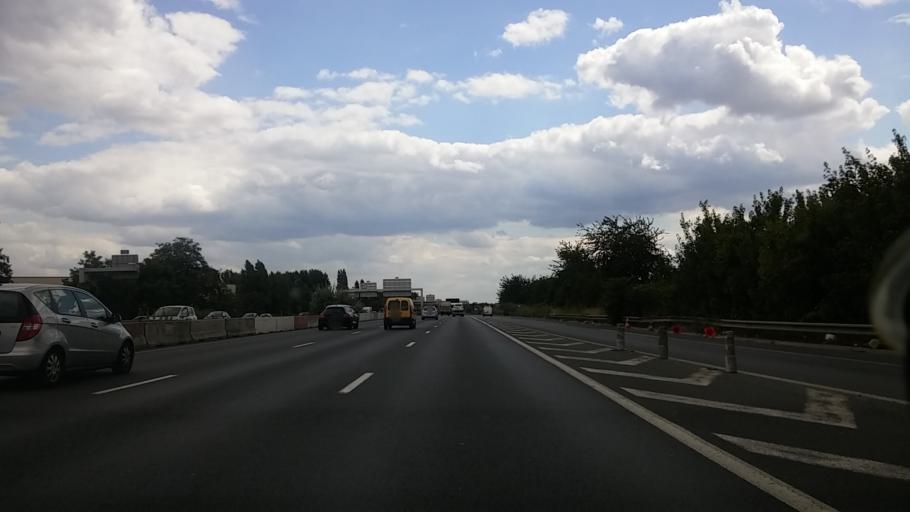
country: FR
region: Ile-de-France
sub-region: Departement de Seine-Saint-Denis
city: Le Blanc-Mesnil
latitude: 48.9482
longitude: 2.4754
